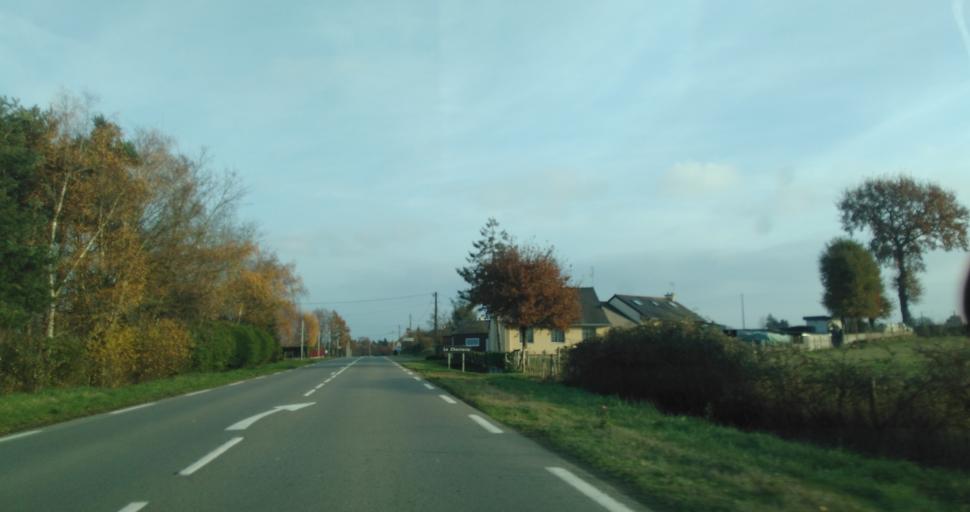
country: FR
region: Brittany
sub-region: Departement d'Ille-et-Vilaine
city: La Chapelle-Thouarault
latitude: 48.1338
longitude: -1.8584
